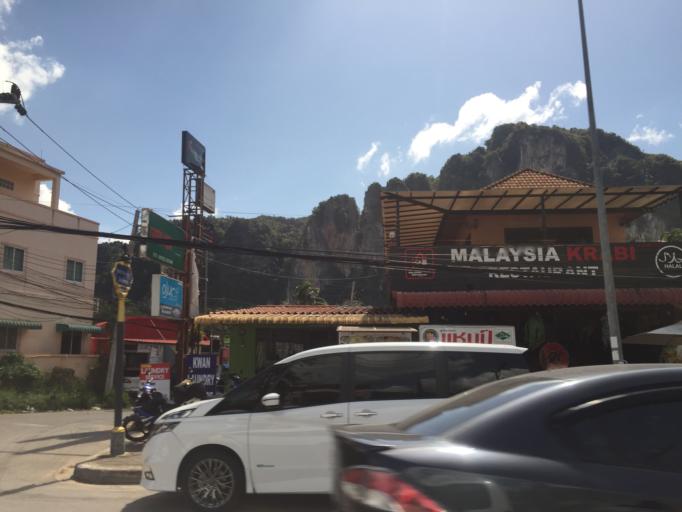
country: TH
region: Phangnga
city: Ban Ao Nang
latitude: 8.0355
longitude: 98.8330
